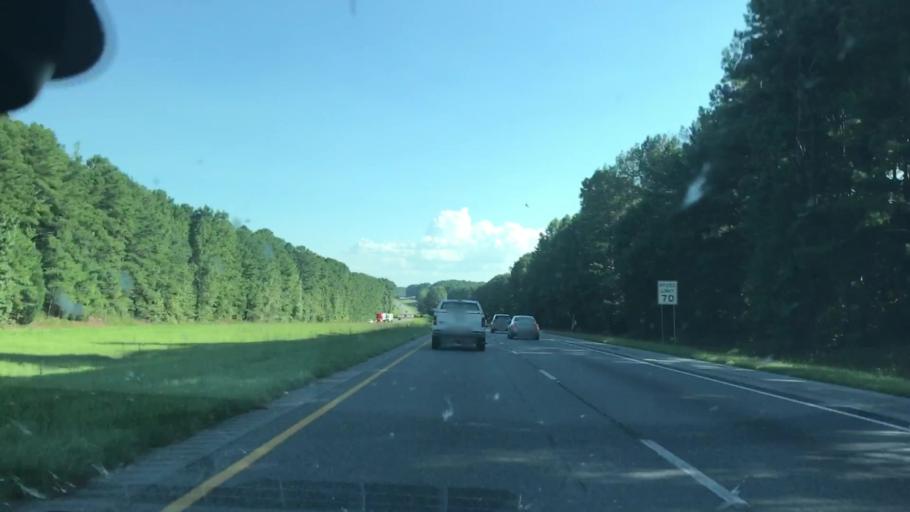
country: US
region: Georgia
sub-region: Harris County
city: Hamilton
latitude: 32.8028
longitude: -85.0215
